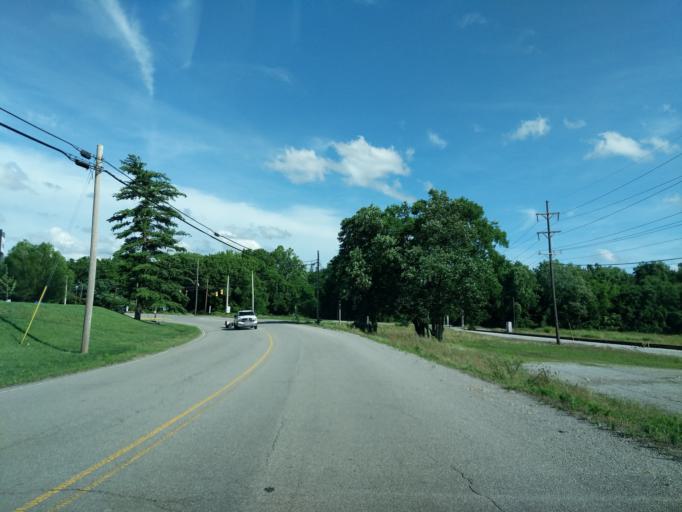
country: US
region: Tennessee
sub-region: Davidson County
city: Lakewood
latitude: 36.2673
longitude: -86.6574
